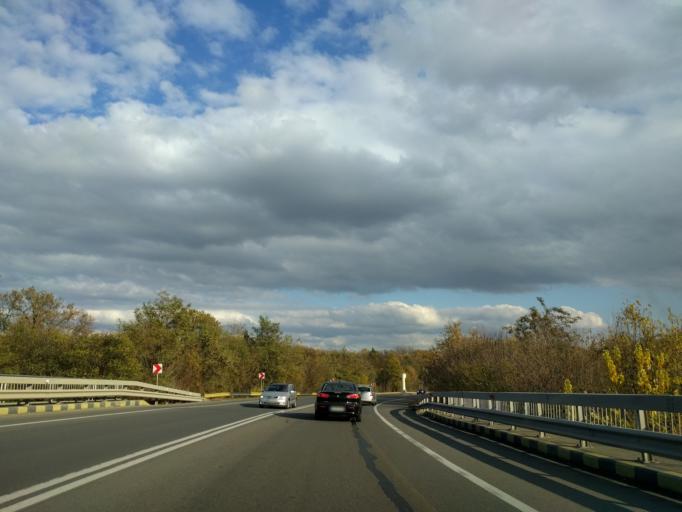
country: RO
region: Ilfov
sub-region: Comuna Branesti
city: Branesti
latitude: 44.4616
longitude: 26.3159
